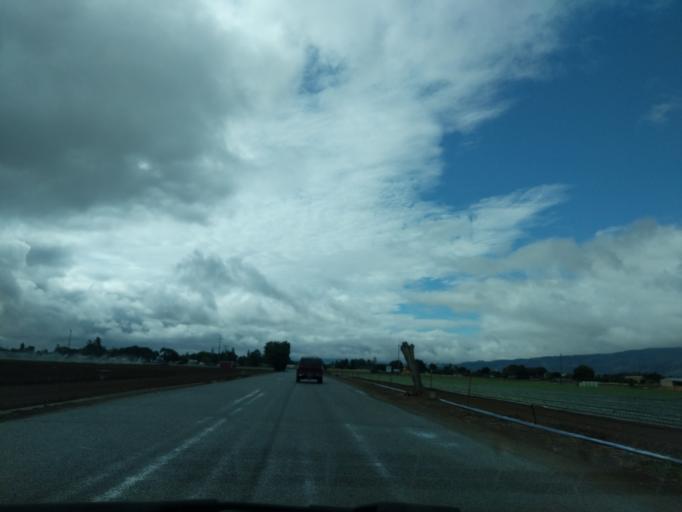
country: US
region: California
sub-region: Santa Clara County
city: San Martin
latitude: 37.0594
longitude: -121.5918
